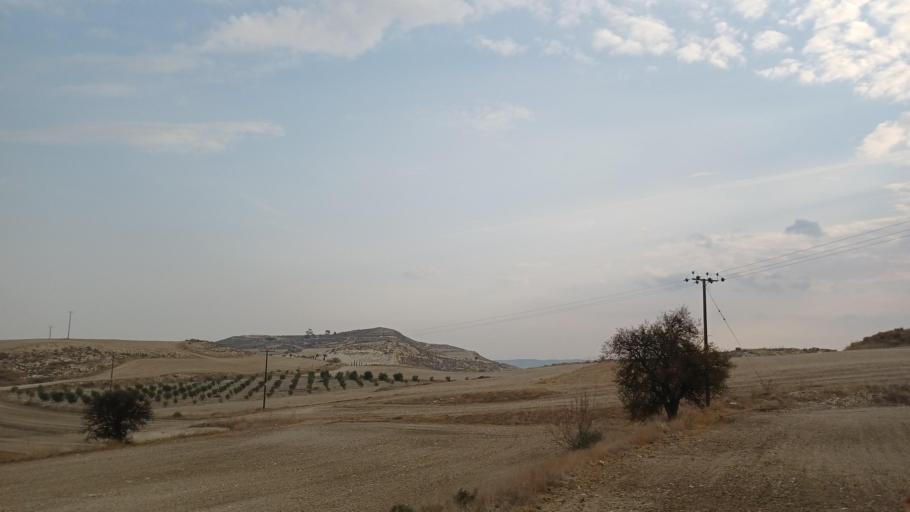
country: CY
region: Larnaka
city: Troulloi
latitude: 35.0297
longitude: 33.5741
